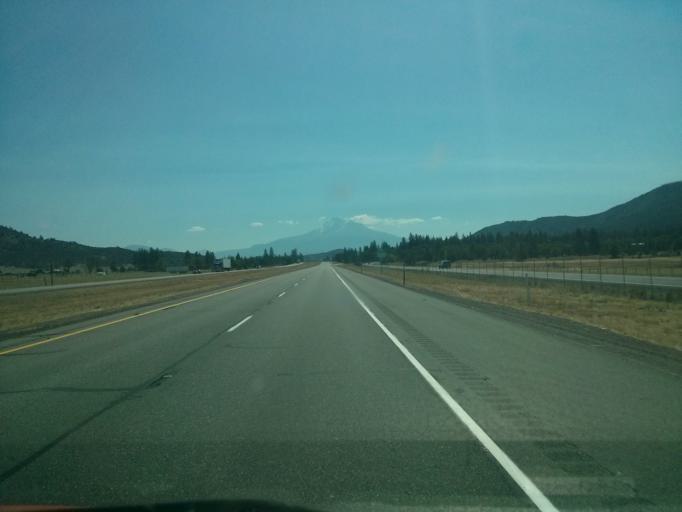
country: US
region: California
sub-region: Siskiyou County
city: Yreka
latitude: 41.6728
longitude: -122.6189
